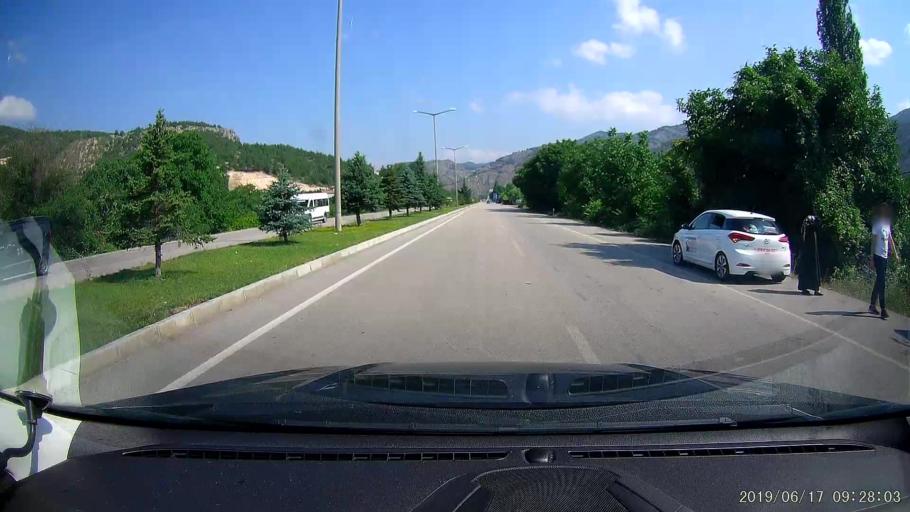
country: TR
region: Amasya
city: Amasya
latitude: 40.6839
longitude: 35.8233
